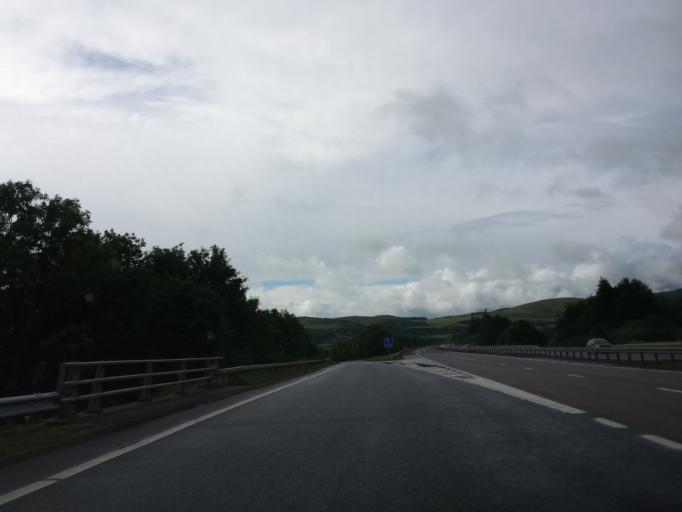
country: GB
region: Scotland
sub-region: Perth and Kinross
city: Bridge of Earn
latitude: 56.3462
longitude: -3.3966
